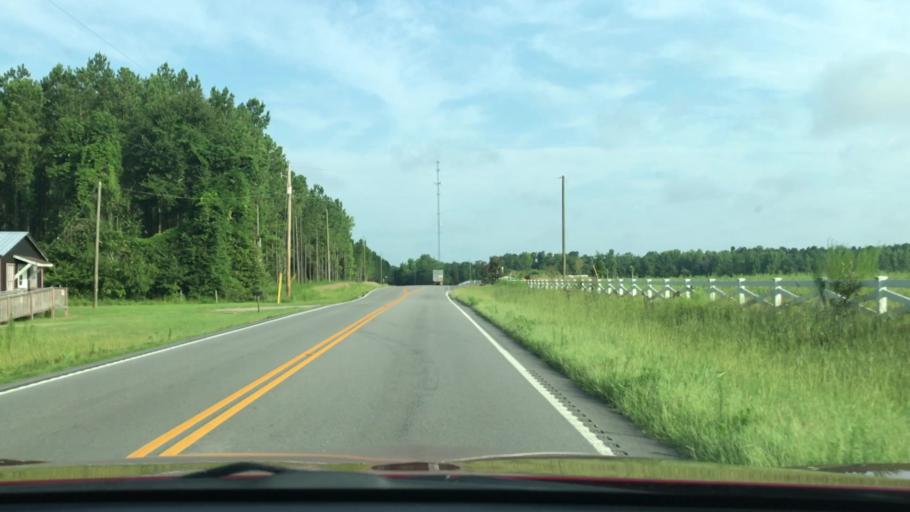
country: US
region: South Carolina
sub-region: Bamberg County
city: Denmark
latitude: 33.5362
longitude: -81.1332
